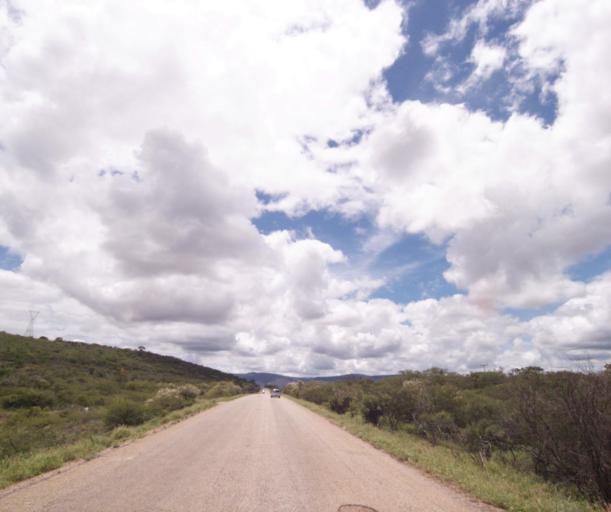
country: BR
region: Bahia
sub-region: Brumado
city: Brumado
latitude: -14.1999
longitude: -41.6079
